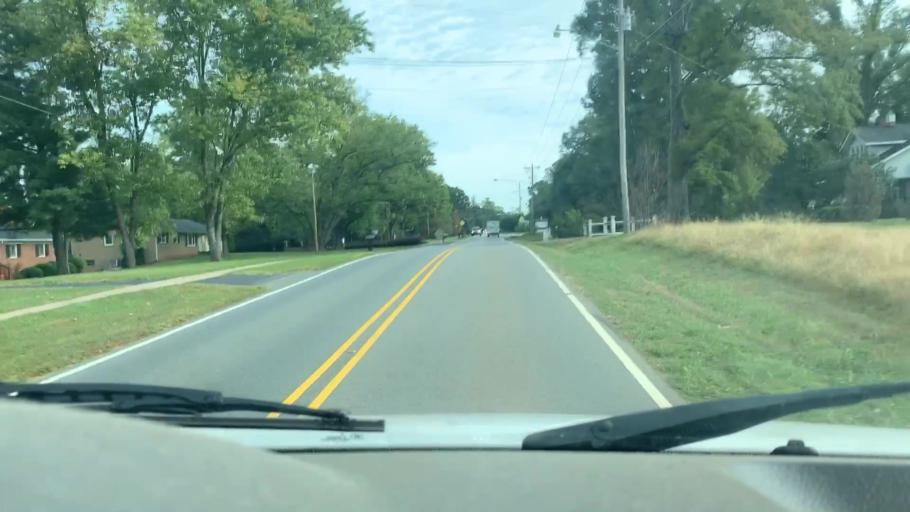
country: US
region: North Carolina
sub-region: Mecklenburg County
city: Cornelius
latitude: 35.4659
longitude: -80.8648
